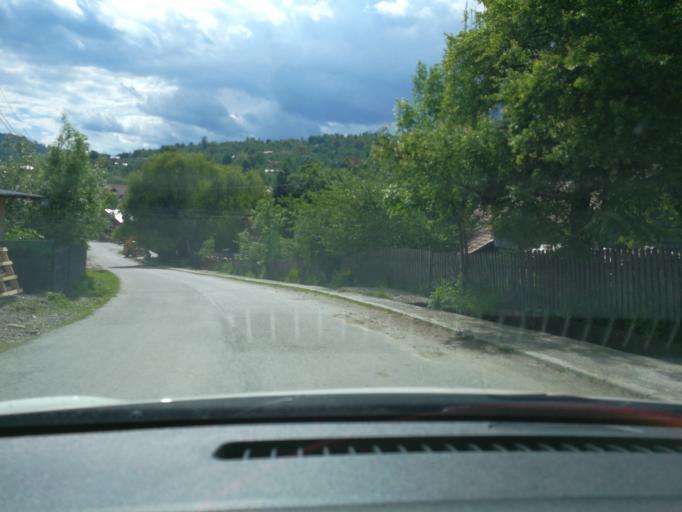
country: RO
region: Prahova
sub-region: Comuna Valea Doftanei
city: Tesila
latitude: 45.3050
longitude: 25.7249
